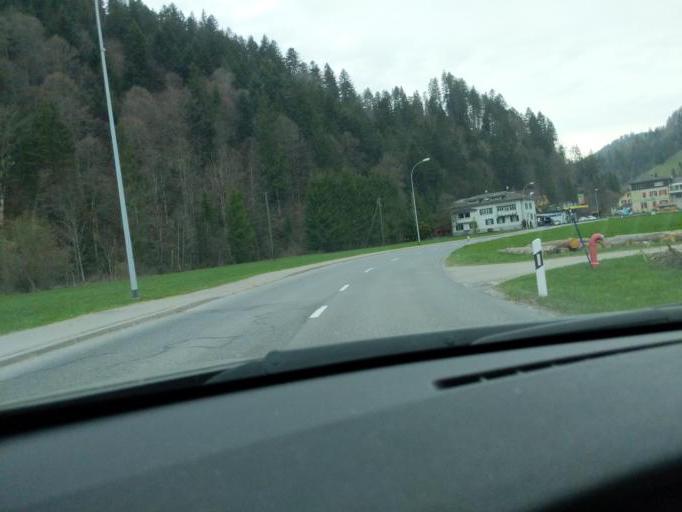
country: CH
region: Lucerne
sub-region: Entlebuch District
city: Escholzmatt
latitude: 46.8967
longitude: 7.9037
